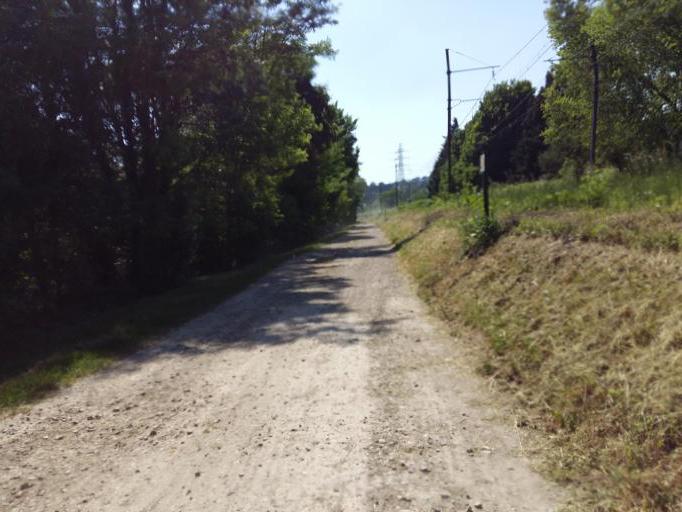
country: FR
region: Rhone-Alpes
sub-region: Departement du Rhone
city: Rillieux-la-Pape
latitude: 45.8051
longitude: 4.9023
